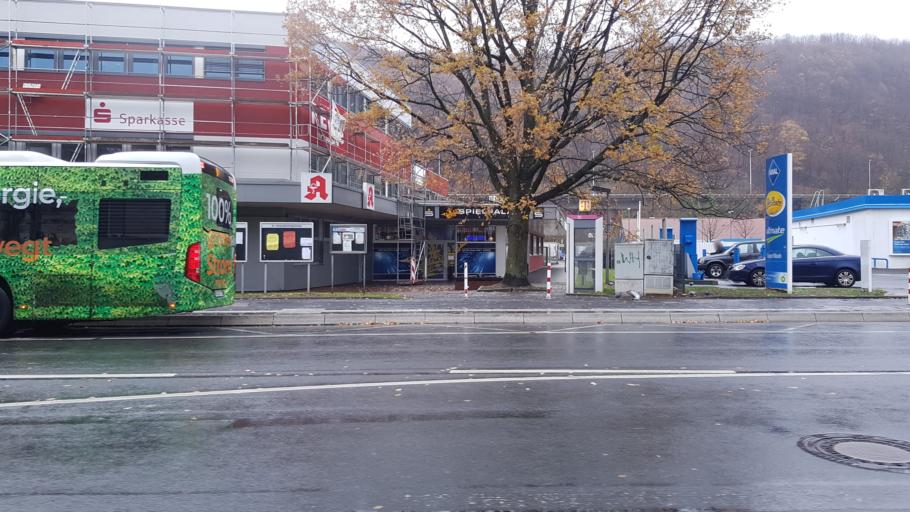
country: DE
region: North Rhine-Westphalia
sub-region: Regierungsbezirk Arnsberg
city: Hagen
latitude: 51.3469
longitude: 7.4946
